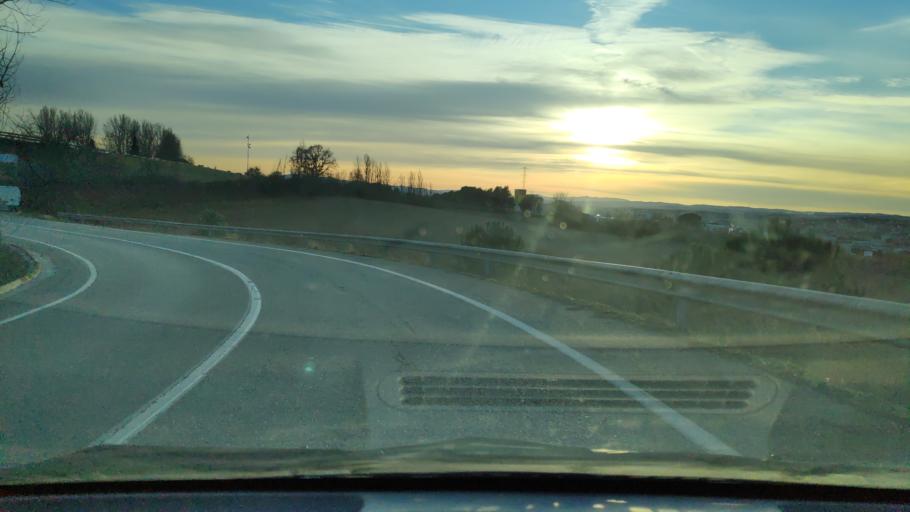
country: ES
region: Catalonia
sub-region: Provincia de Barcelona
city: Llica de Vall
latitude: 41.5754
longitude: 2.2558
